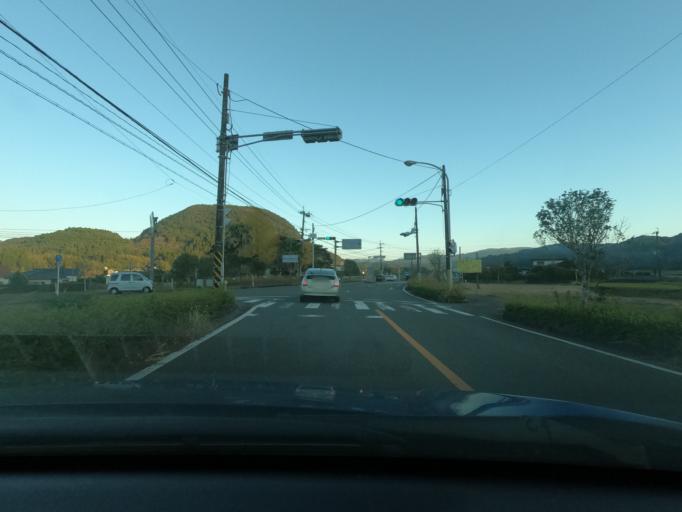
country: JP
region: Kagoshima
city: Satsumasendai
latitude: 31.8040
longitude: 130.3971
